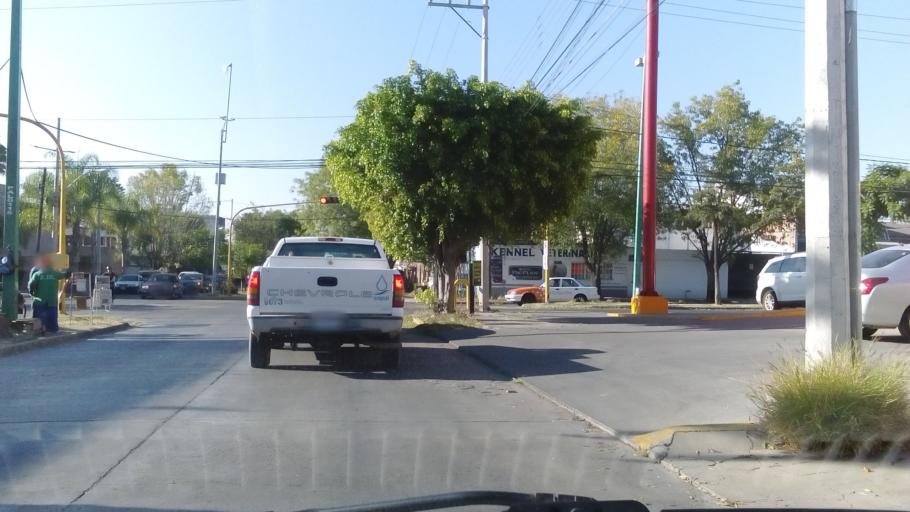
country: MX
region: Guanajuato
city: Leon
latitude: 21.1197
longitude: -101.6986
